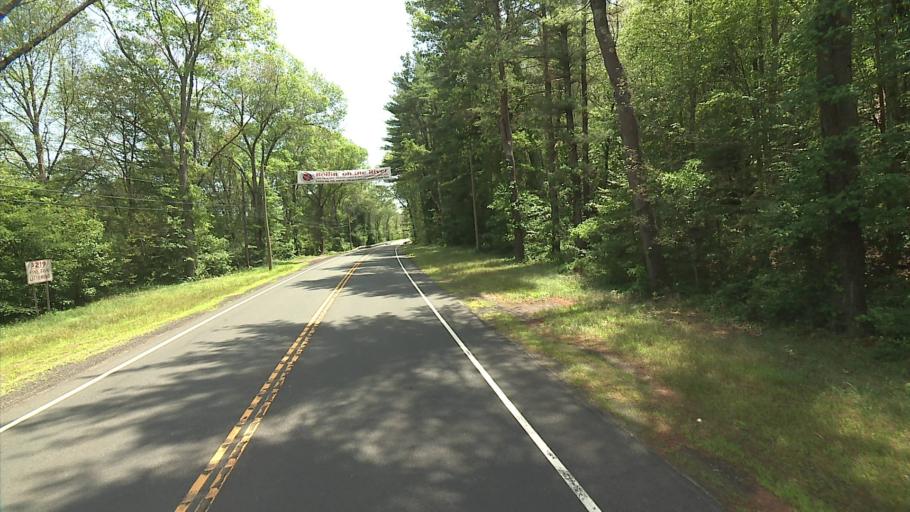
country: US
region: Connecticut
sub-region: Middlesex County
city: Higganum
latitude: 41.4907
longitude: -72.5232
